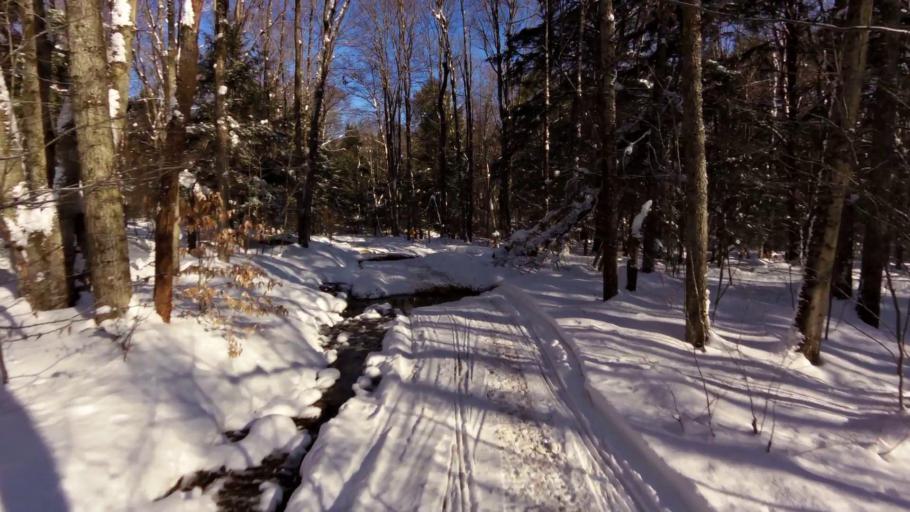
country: US
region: New York
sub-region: Cattaraugus County
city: Salamanca
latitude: 42.0289
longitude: -78.7811
